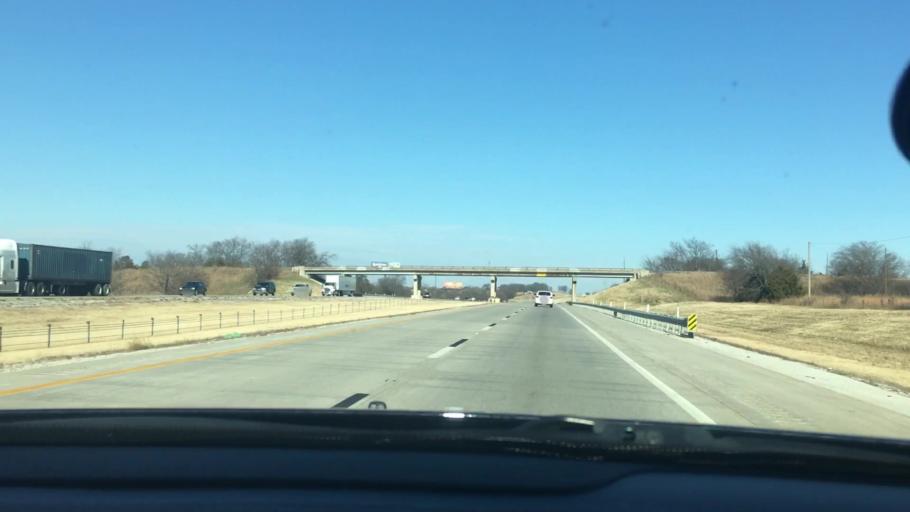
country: US
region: Oklahoma
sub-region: Carter County
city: Ardmore
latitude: 34.1129
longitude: -97.1530
